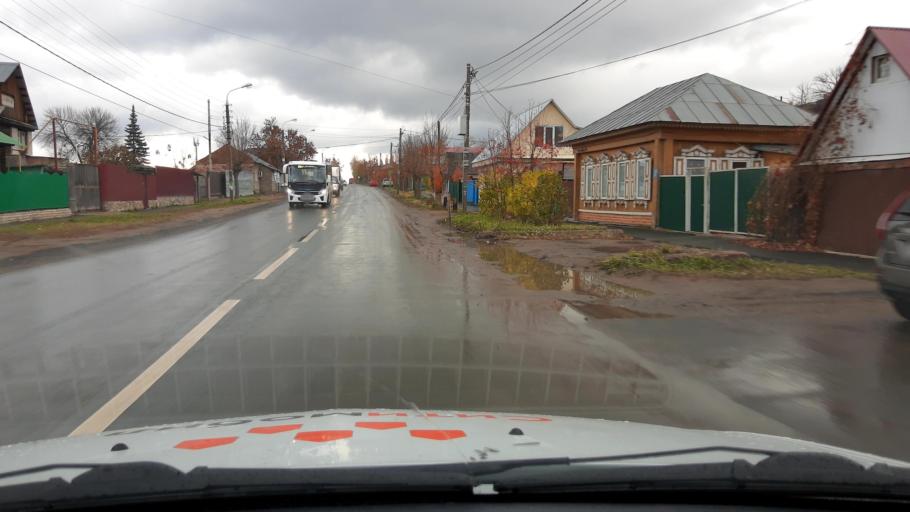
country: RU
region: Bashkortostan
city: Ufa
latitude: 54.7293
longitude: 55.9132
